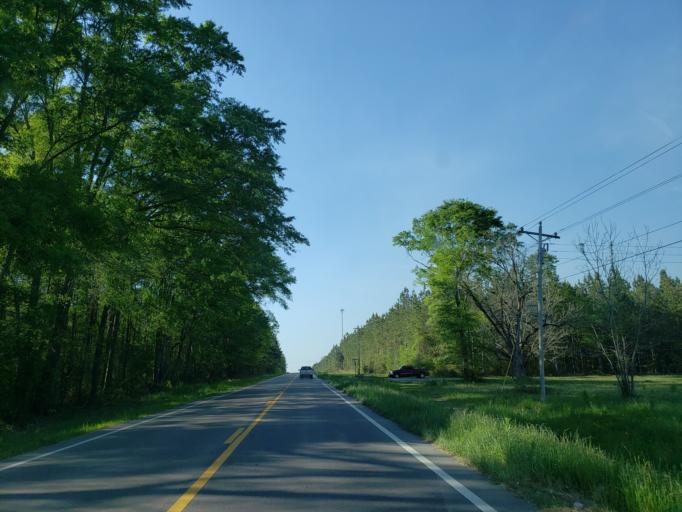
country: US
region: Mississippi
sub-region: Perry County
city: Richton
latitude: 31.4146
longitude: -88.9555
